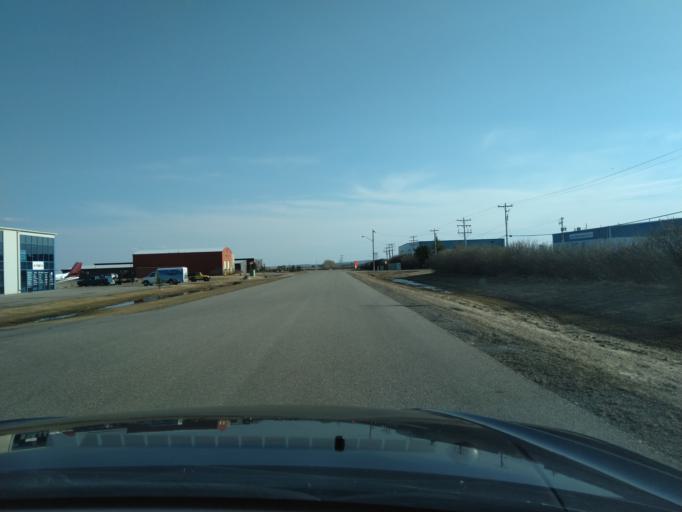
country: CA
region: Alberta
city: Cochrane
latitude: 51.0995
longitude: -114.3738
